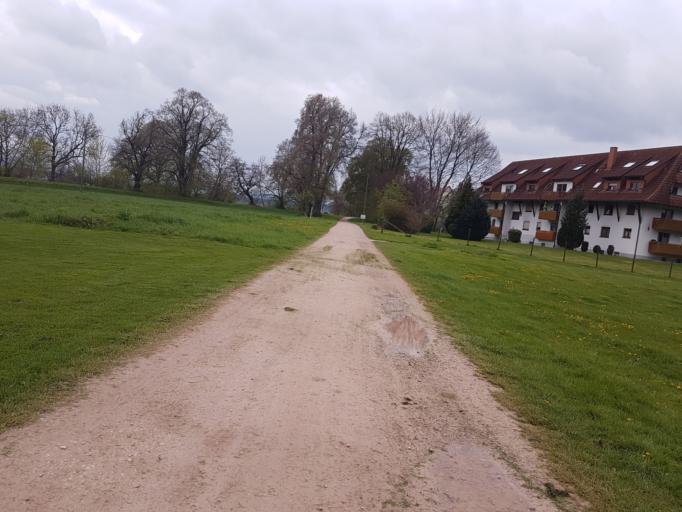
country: DE
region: Baden-Wuerttemberg
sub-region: Freiburg Region
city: Donaueschingen
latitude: 47.9429
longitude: 8.5061
